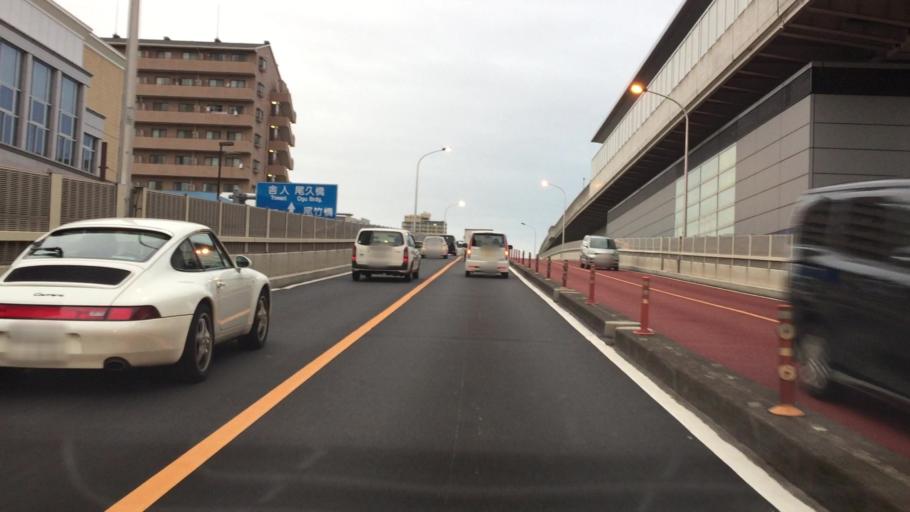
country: JP
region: Saitama
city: Soka
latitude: 35.7480
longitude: 139.7697
